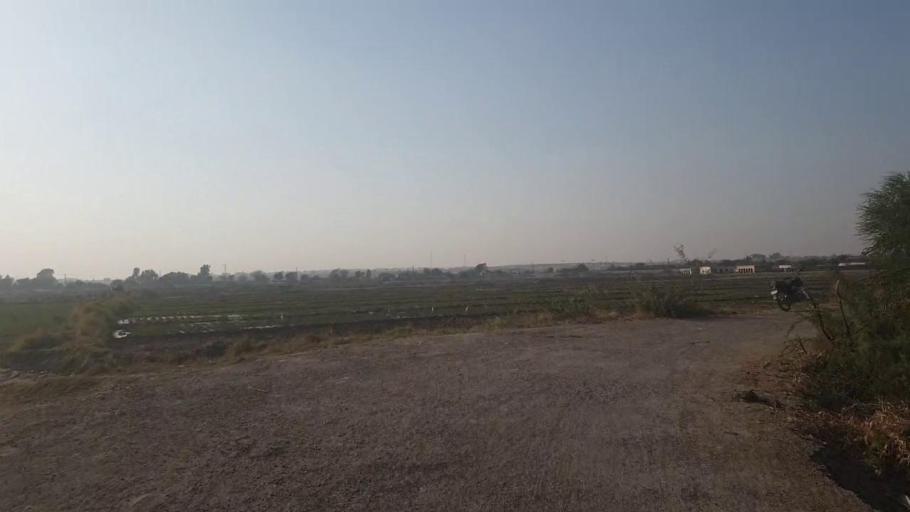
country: PK
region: Sindh
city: Kotri
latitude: 25.3928
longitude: 68.2906
